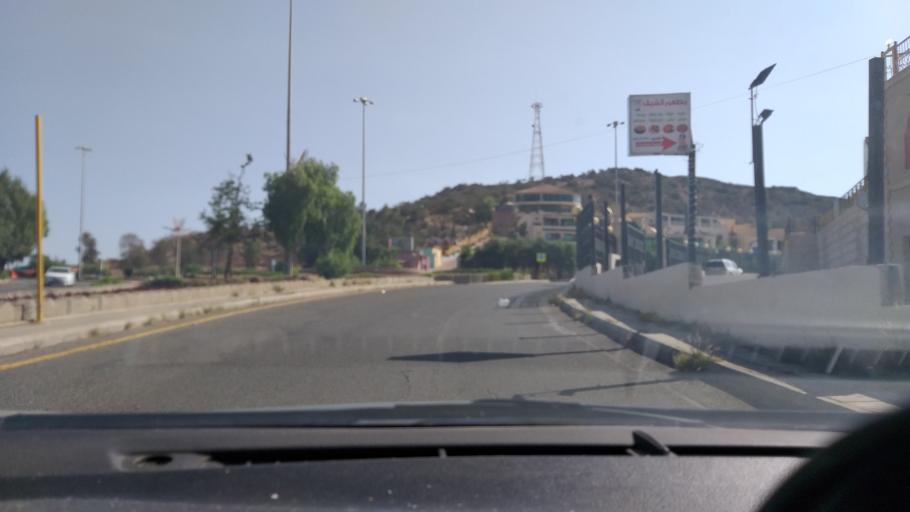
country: SA
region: Makkah
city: Ash Shafa
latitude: 21.0801
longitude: 40.3152
